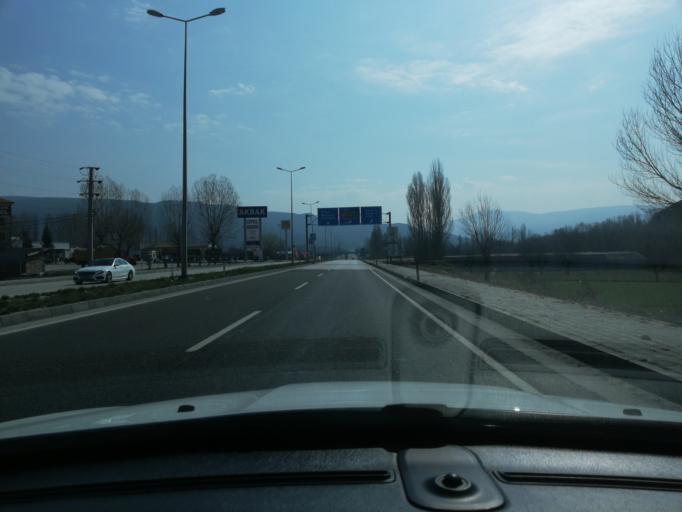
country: TR
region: Cankiri
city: Ilgaz
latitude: 40.9064
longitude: 33.6439
